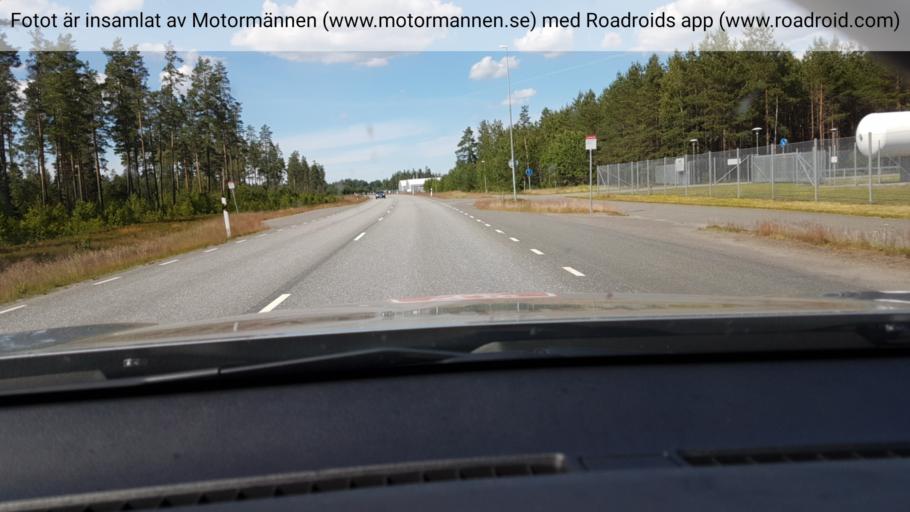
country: SE
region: Joenkoeping
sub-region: Vaggeryds Kommun
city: Skillingaryd
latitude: 57.4601
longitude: 14.0947
